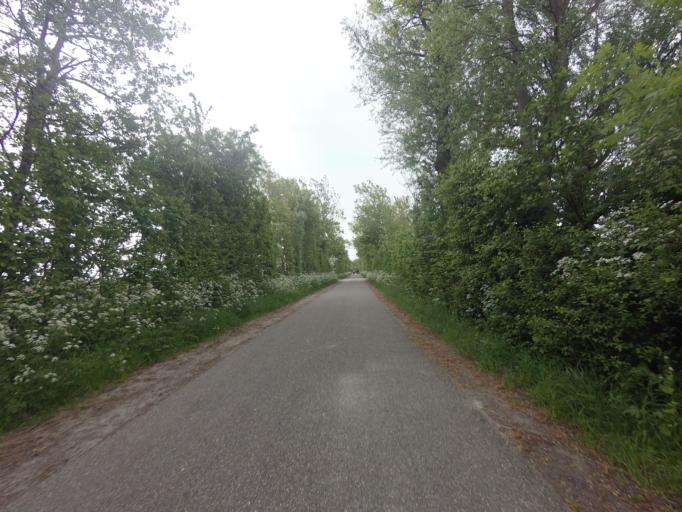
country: NL
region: Zeeland
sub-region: Gemeente Middelburg
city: Middelburg
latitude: 51.5314
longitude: 3.5679
